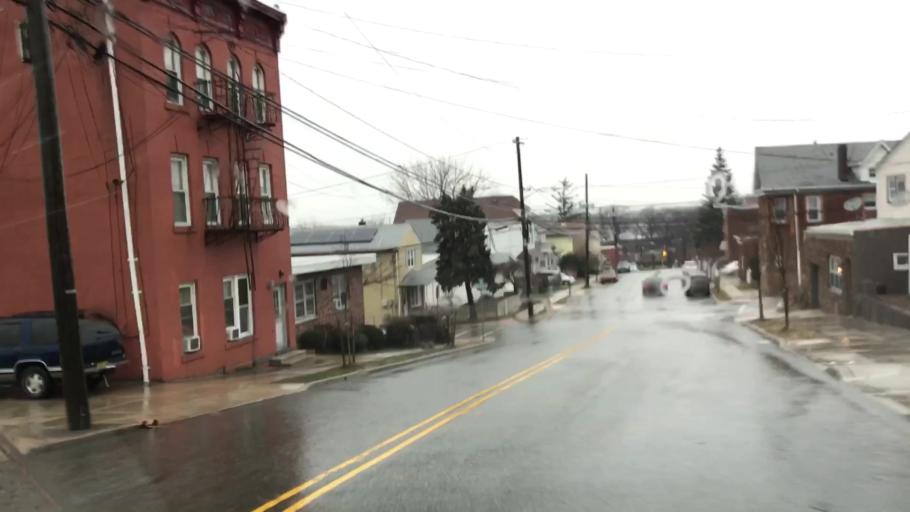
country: US
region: New Jersey
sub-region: Bergen County
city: Garfield
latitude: 40.8797
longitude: -74.1122
